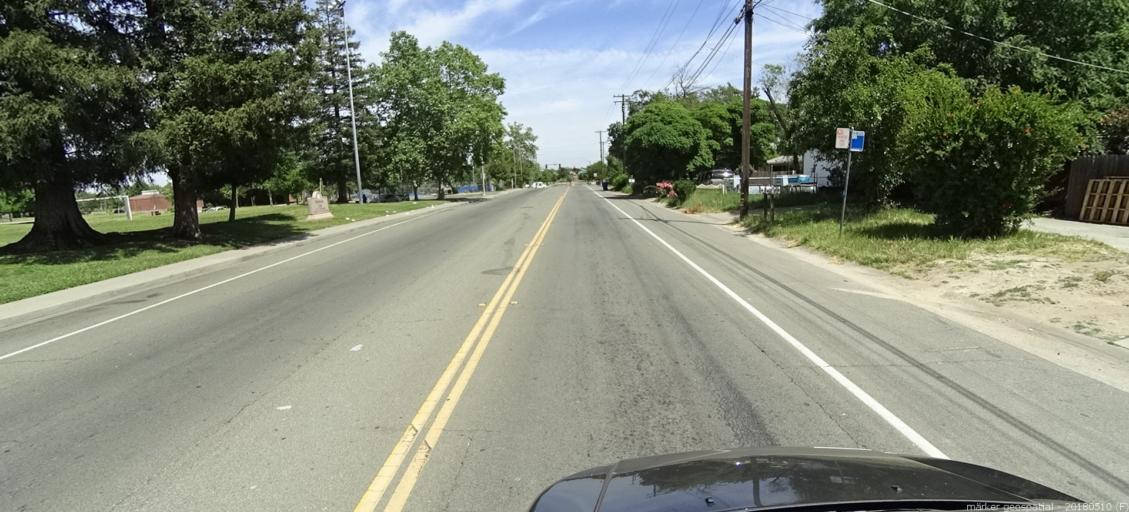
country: US
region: California
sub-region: Sacramento County
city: Sacramento
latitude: 38.6302
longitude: -121.4589
